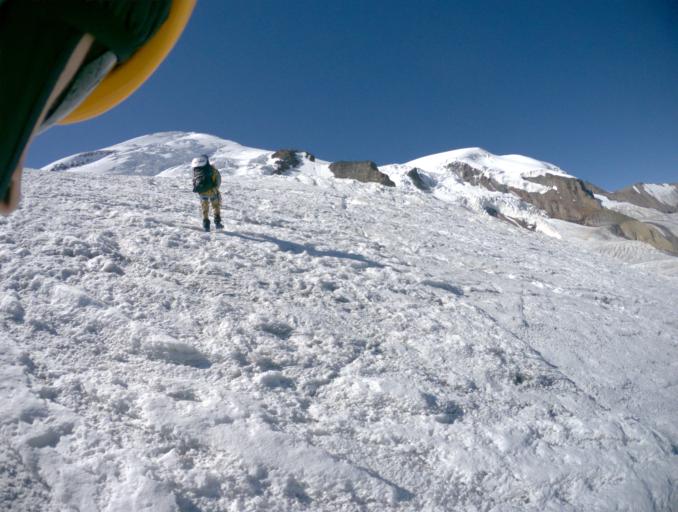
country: RU
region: Kabardino-Balkariya
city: Terskol
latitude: 43.3863
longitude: 42.4363
